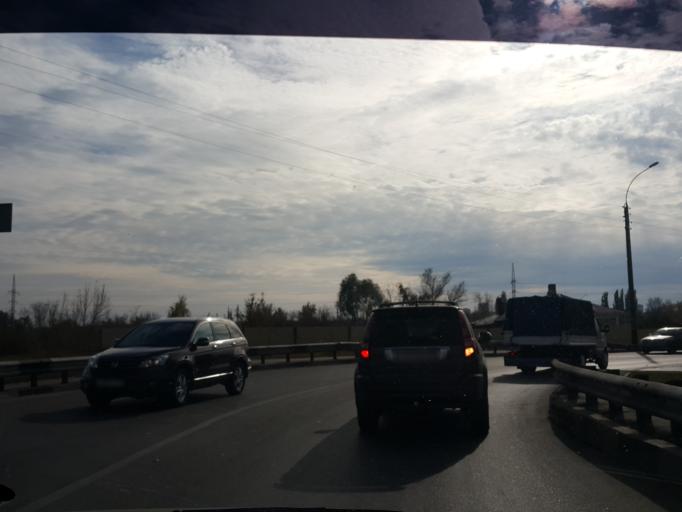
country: RU
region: Tambov
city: Tambov
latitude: 52.7296
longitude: 41.4631
